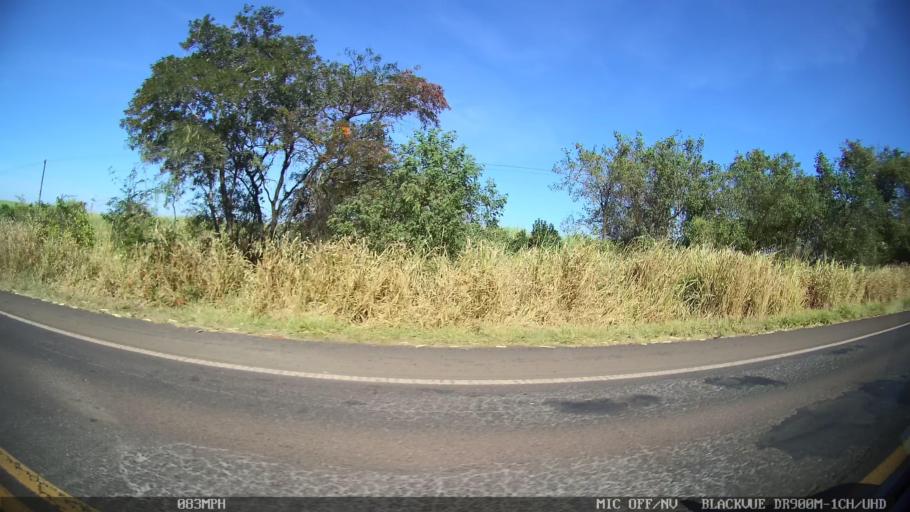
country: BR
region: Sao Paulo
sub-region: Barretos
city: Barretos
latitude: -20.5508
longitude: -48.6337
